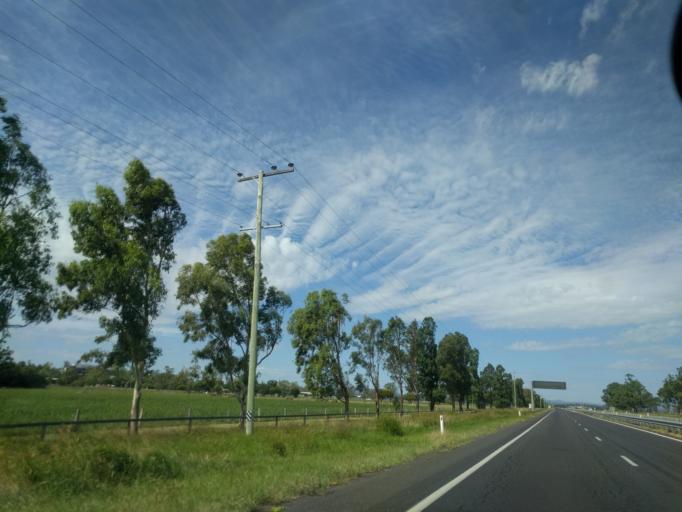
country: AU
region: Queensland
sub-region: Lockyer Valley
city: Gatton
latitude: -27.5464
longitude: 152.3372
